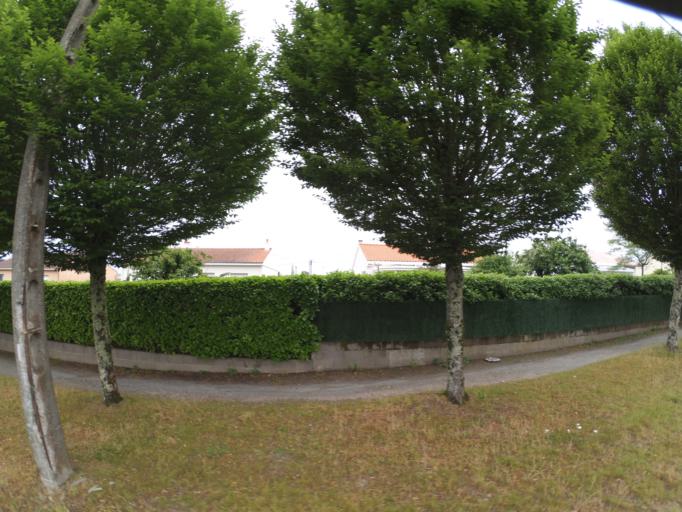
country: FR
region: Pays de la Loire
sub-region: Departement de la Vendee
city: La Roche-sur-Yon
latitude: 46.6523
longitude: -1.4335
